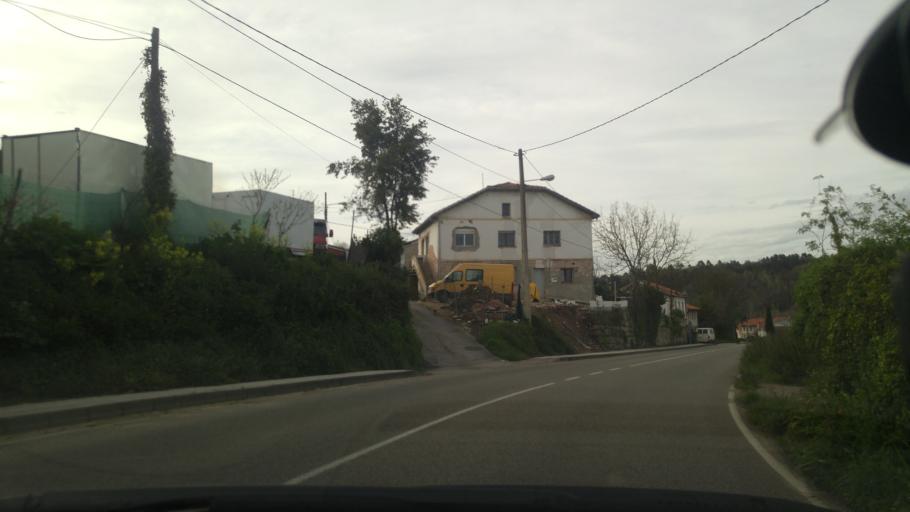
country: ES
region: Asturias
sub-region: Province of Asturias
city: Corvera de Asturias
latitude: 43.5237
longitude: -5.8718
